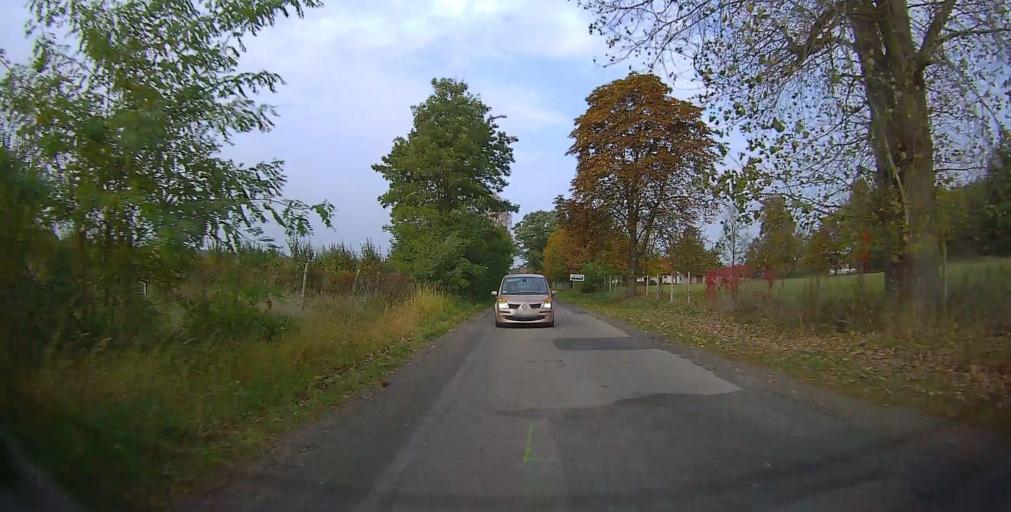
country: PL
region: Masovian Voivodeship
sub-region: Powiat grojecki
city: Mogielnica
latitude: 51.6549
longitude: 20.7203
